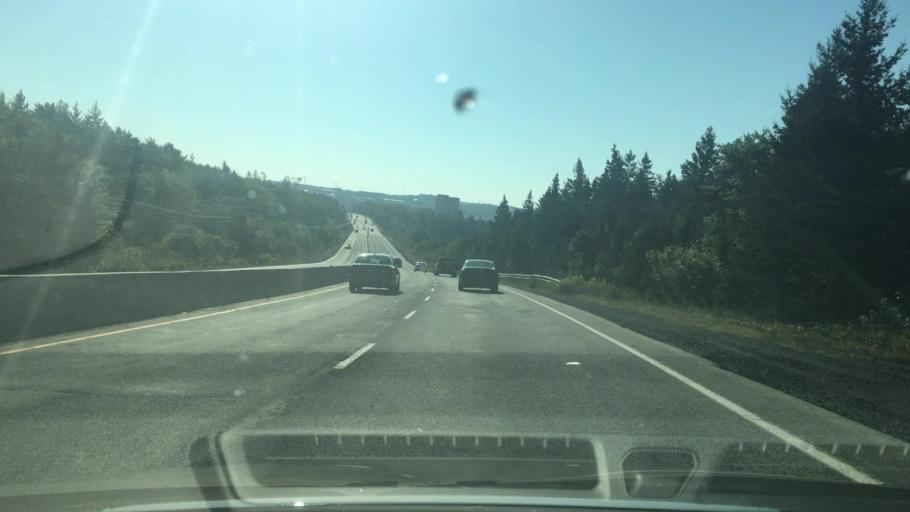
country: CA
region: Nova Scotia
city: Dartmouth
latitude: 44.7089
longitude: -63.6245
